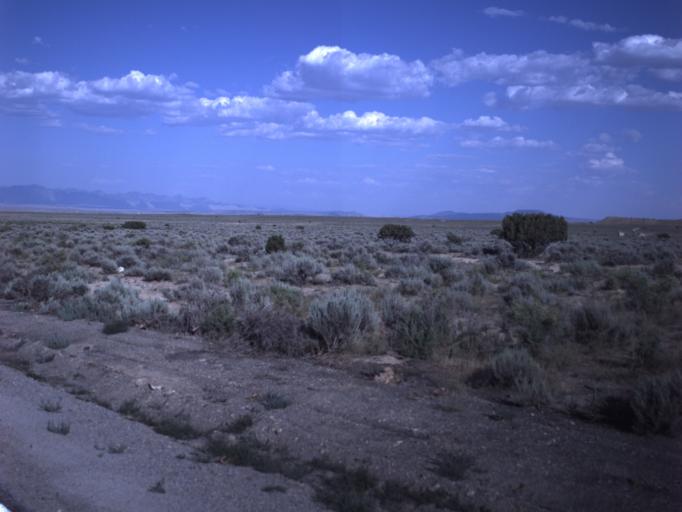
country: US
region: Utah
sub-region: Carbon County
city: Price
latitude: 39.4852
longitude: -110.8839
